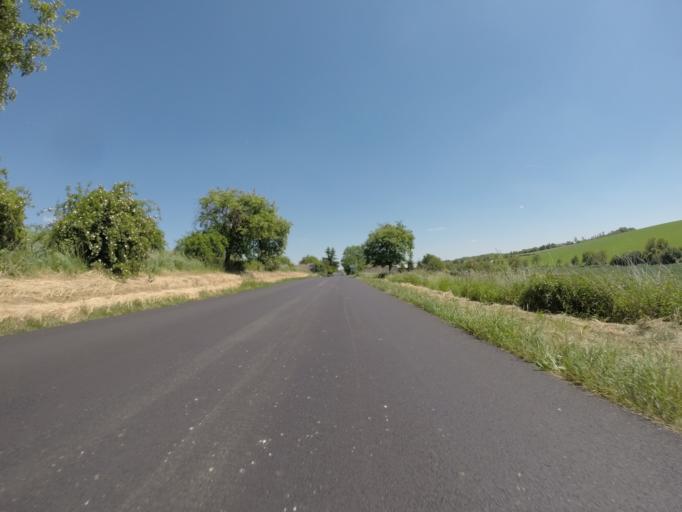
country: SK
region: Trnavsky
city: Hlohovec
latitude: 48.4689
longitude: 17.9046
